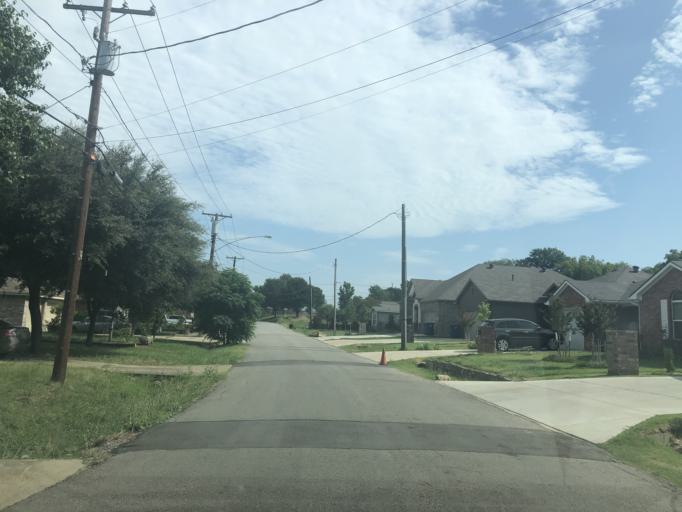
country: US
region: Texas
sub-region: Dallas County
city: Dallas
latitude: 32.8151
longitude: -96.8557
